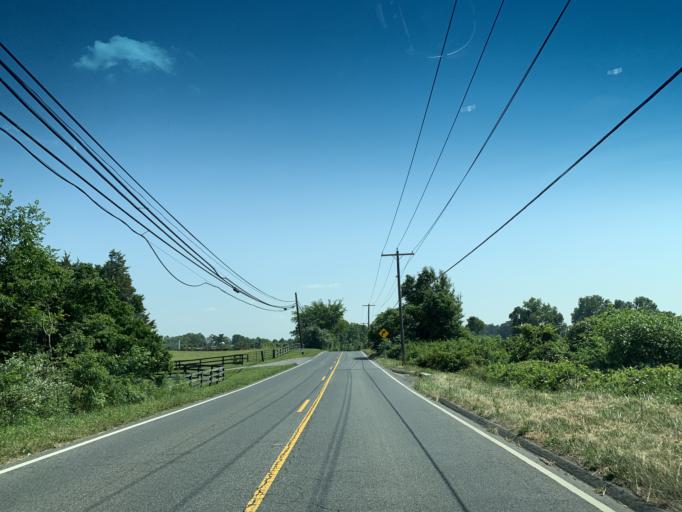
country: US
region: Maryland
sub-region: Montgomery County
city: Poolesville
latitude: 39.1659
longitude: -77.4177
